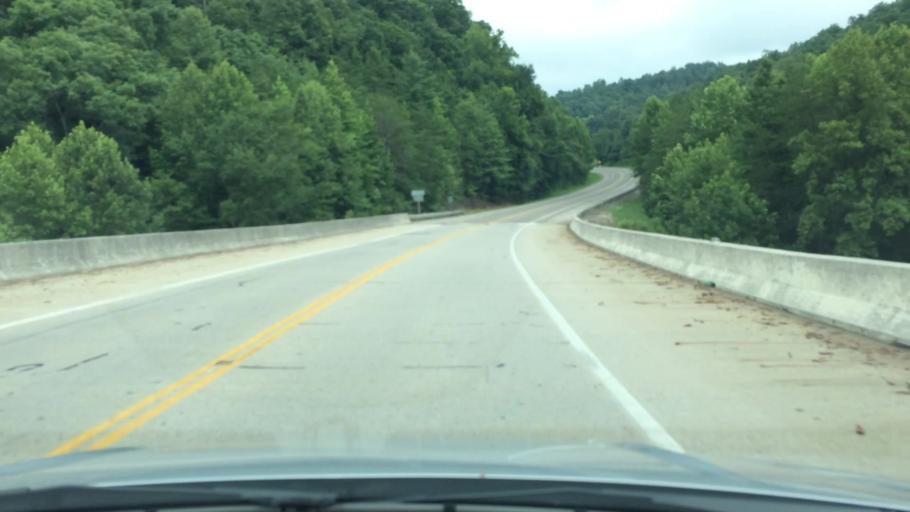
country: US
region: Tennessee
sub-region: Scott County
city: Huntsville
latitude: 36.4040
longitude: -84.4507
